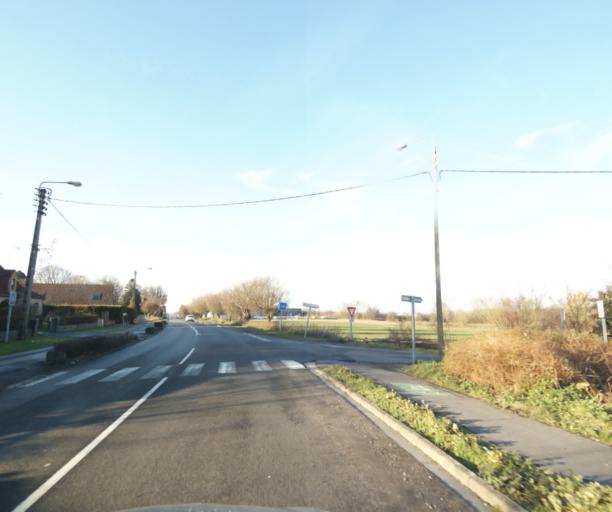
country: FR
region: Nord-Pas-de-Calais
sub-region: Departement du Nord
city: Saultain
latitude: 50.3383
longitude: 3.5718
